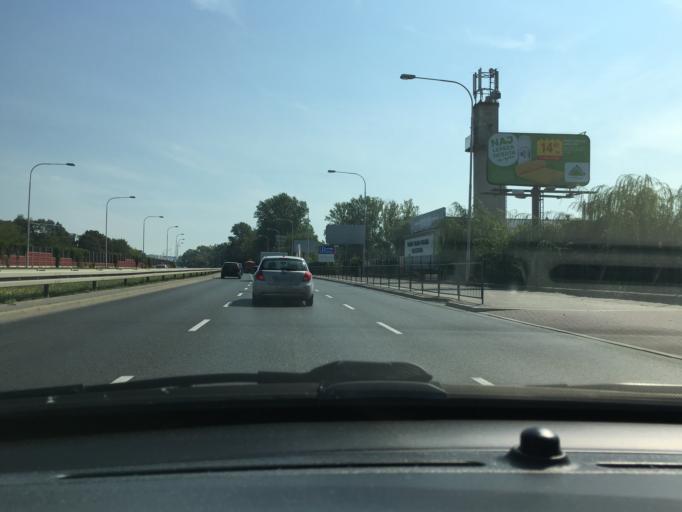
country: PL
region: Masovian Voivodeship
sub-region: Warszawa
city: Praga Poludnie
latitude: 52.2219
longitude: 21.0647
